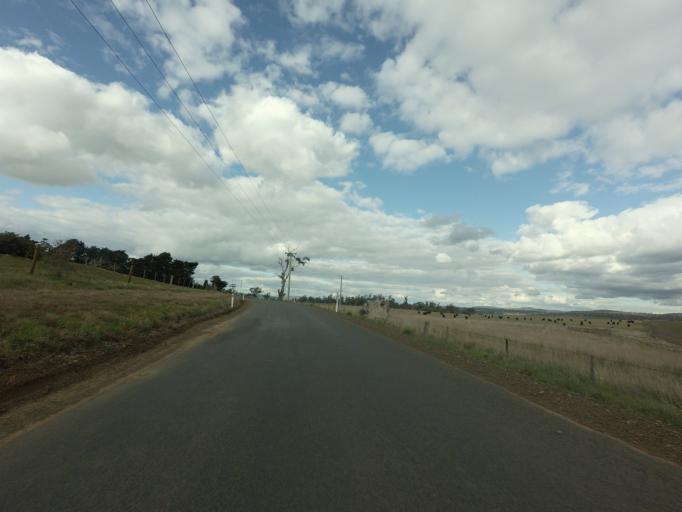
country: AU
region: Tasmania
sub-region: Northern Midlands
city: Longford
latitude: -41.8060
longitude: 147.1545
